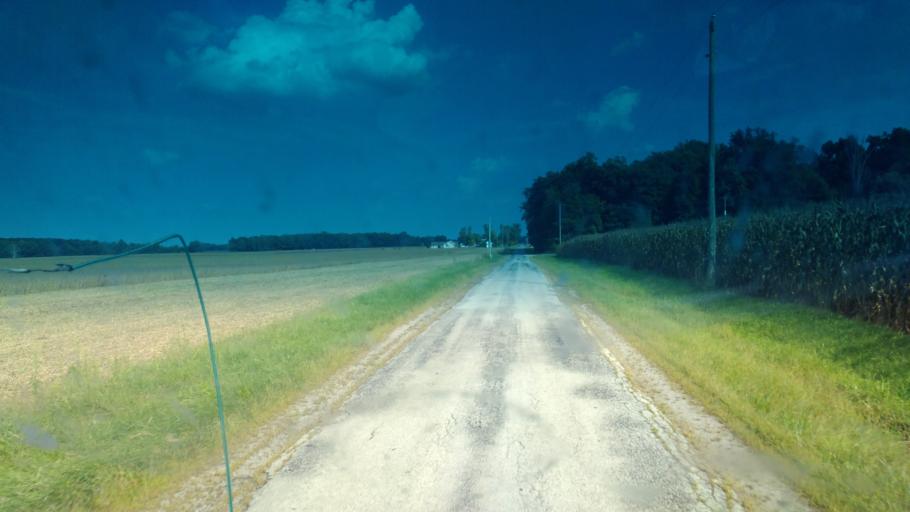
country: US
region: Ohio
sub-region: Hancock County
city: Arlington
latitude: 40.8191
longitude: -83.5992
